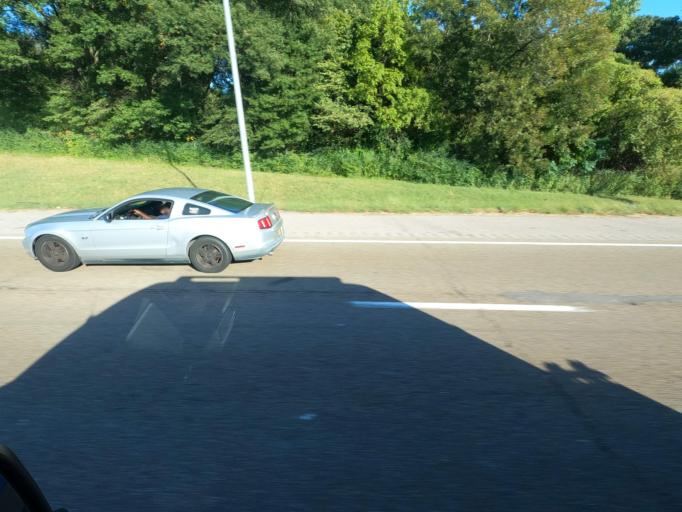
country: US
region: Tennessee
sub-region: Shelby County
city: New South Memphis
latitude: 35.0748
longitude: -90.0256
